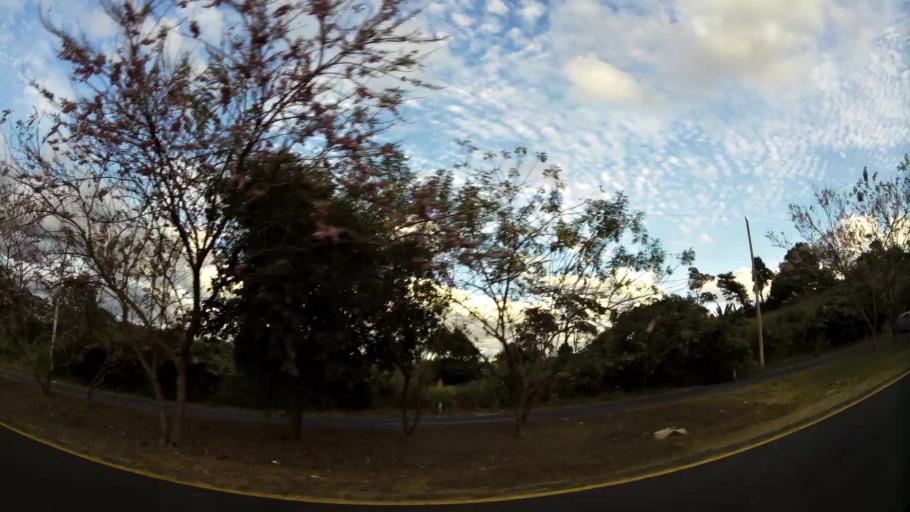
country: SV
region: San Vicente
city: San Sebastian
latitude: 13.6965
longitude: -88.8483
